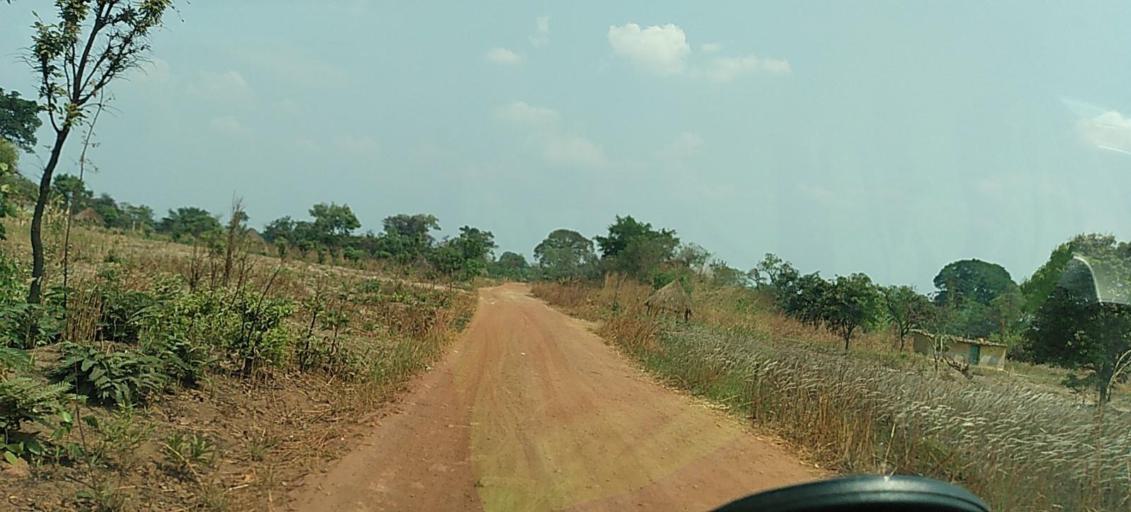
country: ZM
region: North-Western
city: Kansanshi
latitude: -12.1025
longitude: 26.3647
